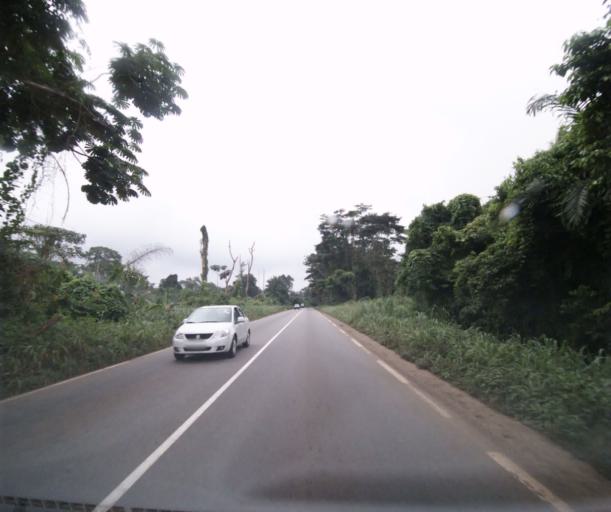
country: CM
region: Centre
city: Eseka
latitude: 3.8744
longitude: 10.6728
